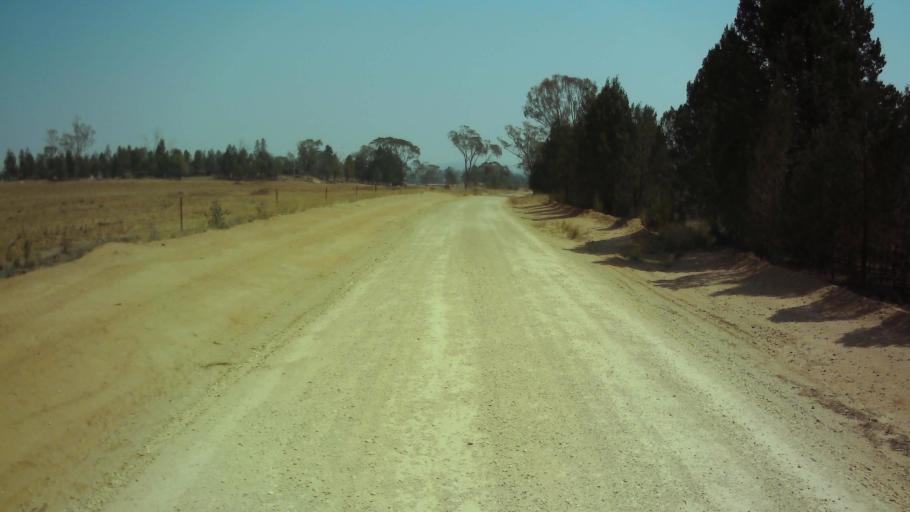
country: AU
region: New South Wales
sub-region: Weddin
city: Grenfell
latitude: -33.6530
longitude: 148.2717
